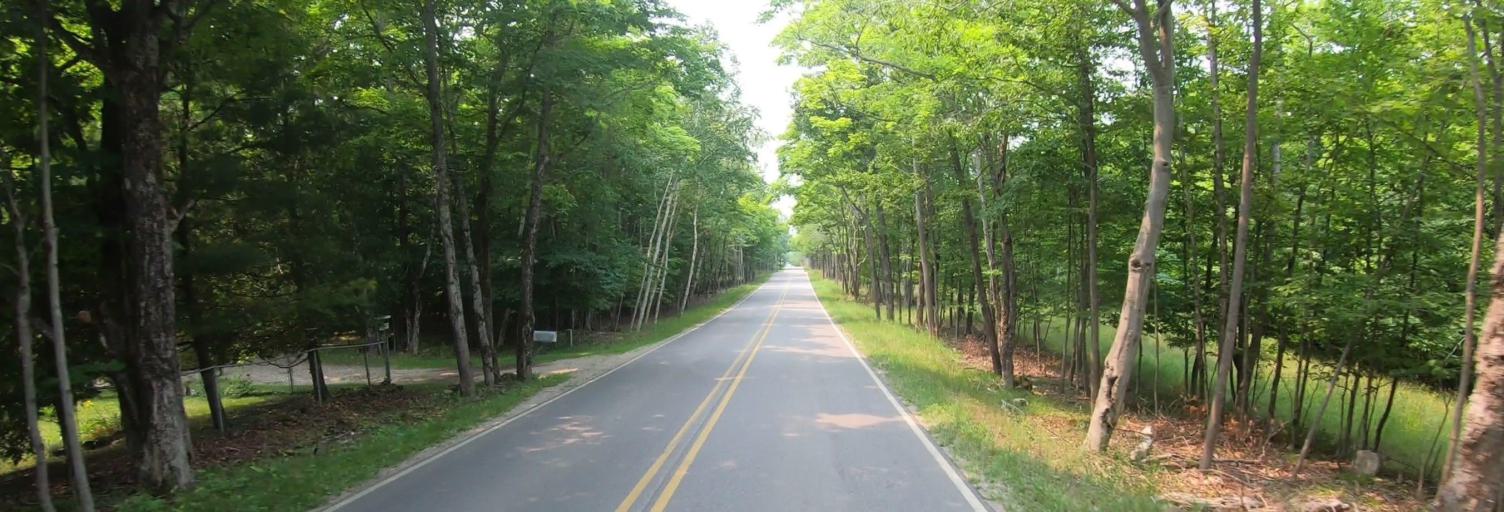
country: CA
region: Ontario
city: Thessalon
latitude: 46.0204
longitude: -83.7243
